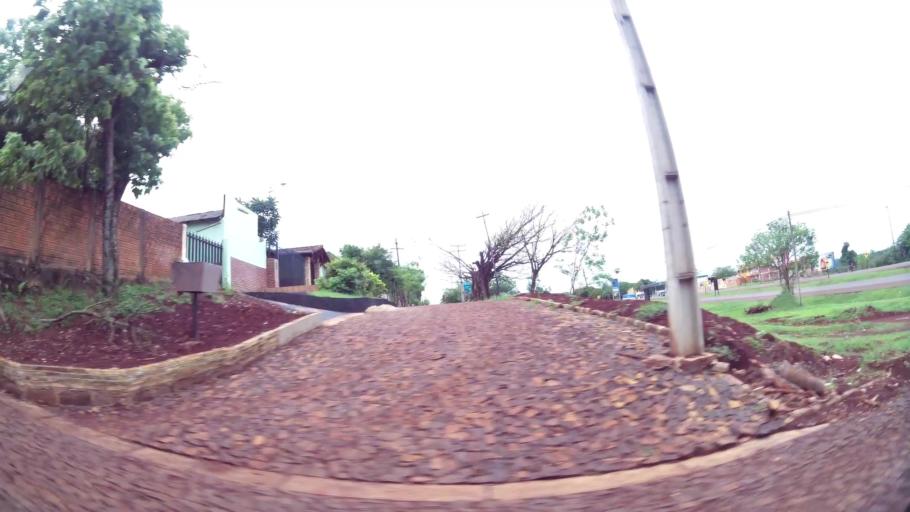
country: PY
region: Alto Parana
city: Presidente Franco
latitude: -25.4890
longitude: -54.7968
